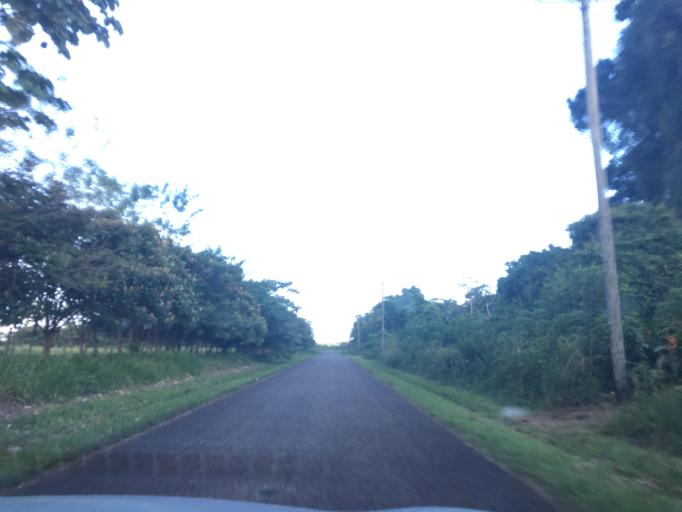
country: BZ
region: Stann Creek
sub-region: Dangriga
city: Dangriga
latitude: 16.8280
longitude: -88.3482
